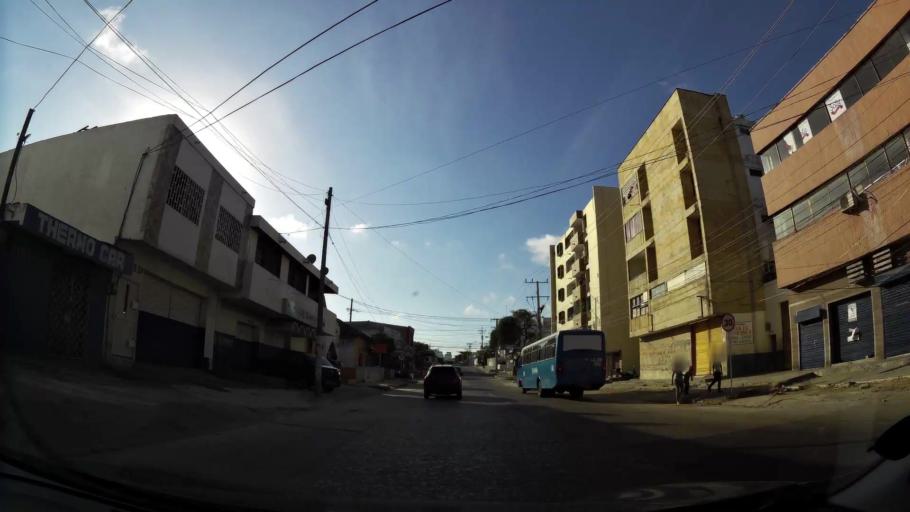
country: CO
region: Atlantico
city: Barranquilla
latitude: 10.9849
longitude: -74.7935
